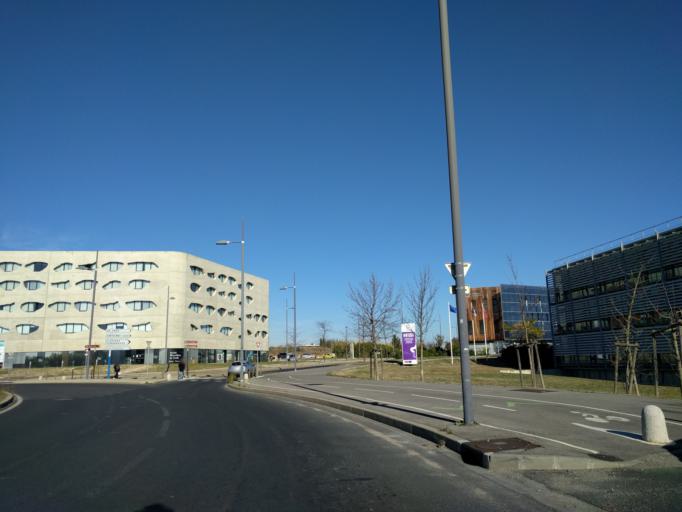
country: FR
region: Languedoc-Roussillon
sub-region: Departement de l'Herault
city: Castelnau-le-Lez
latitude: 43.6185
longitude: 3.9137
